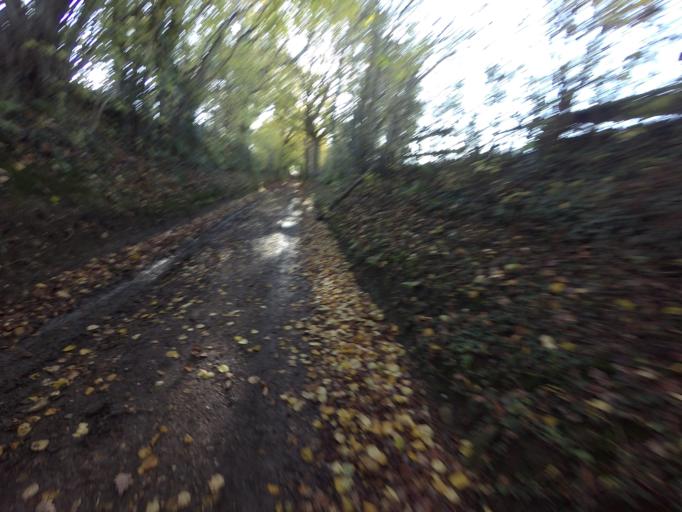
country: NL
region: Limburg
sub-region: Eijsden-Margraten
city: Margraten
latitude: 50.7971
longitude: 5.8685
